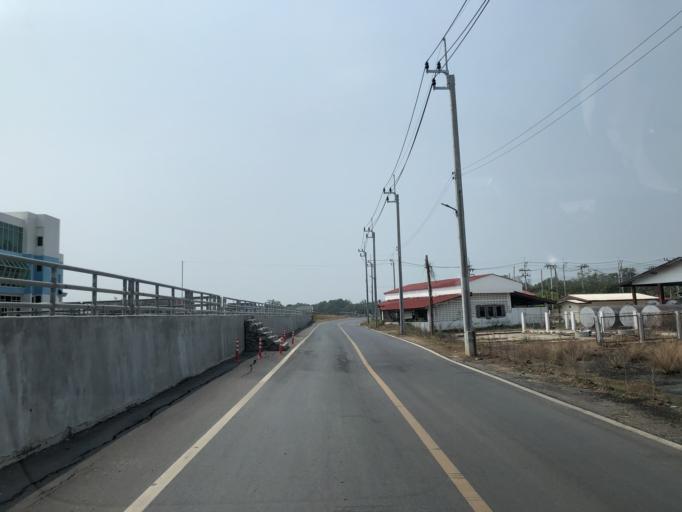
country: TH
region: Samut Prakan
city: Bang Bo
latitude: 13.5181
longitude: 100.8226
